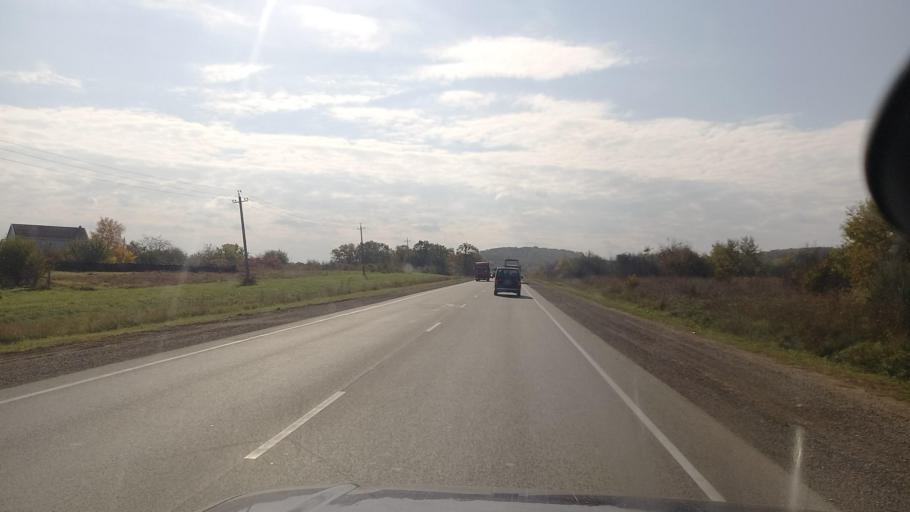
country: RU
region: Krasnodarskiy
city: Abinsk
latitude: 44.8571
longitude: 38.1332
